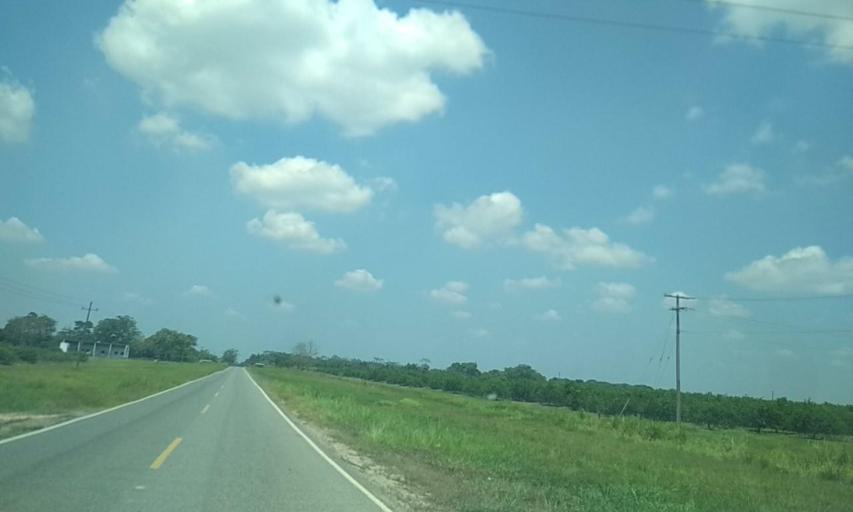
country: MX
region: Tabasco
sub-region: Huimanguillo
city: Huapacal 1ra. Seccion
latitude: 17.7519
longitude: -93.6653
